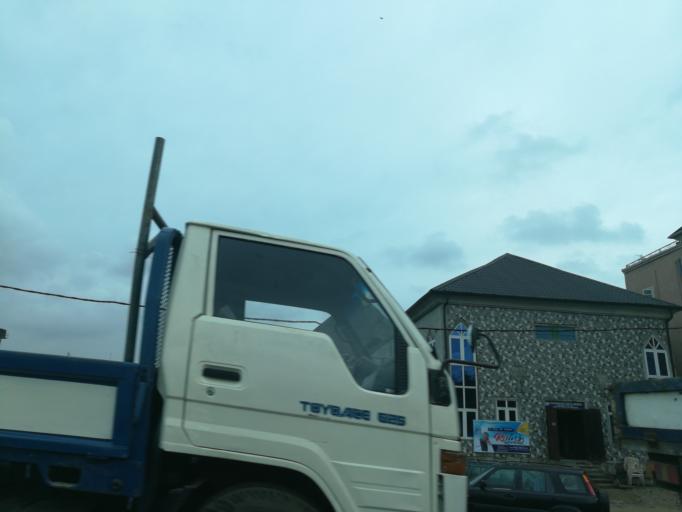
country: NG
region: Rivers
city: Port Harcourt
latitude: 4.8095
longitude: 6.9933
